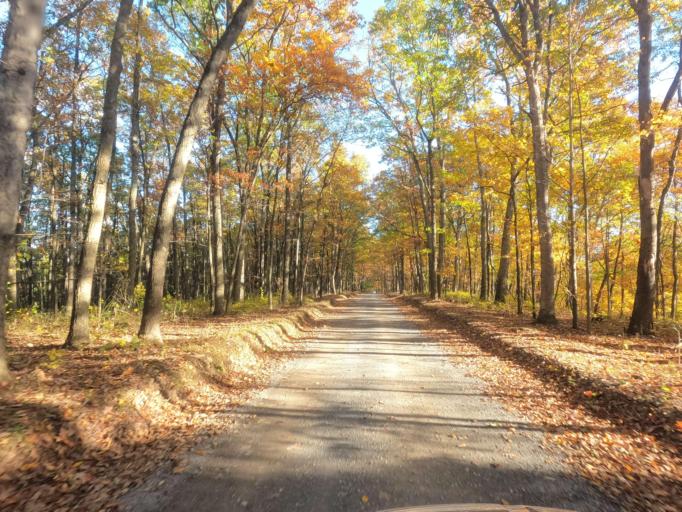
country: US
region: West Virginia
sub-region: Morgan County
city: Berkeley Springs
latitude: 39.6552
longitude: -78.4627
